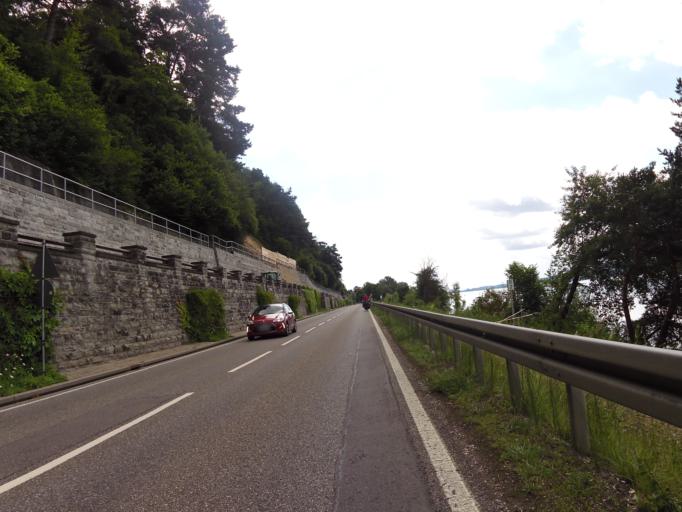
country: DE
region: Baden-Wuerttemberg
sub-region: Tuebingen Region
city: Sipplingen
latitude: 47.8026
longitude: 9.0804
